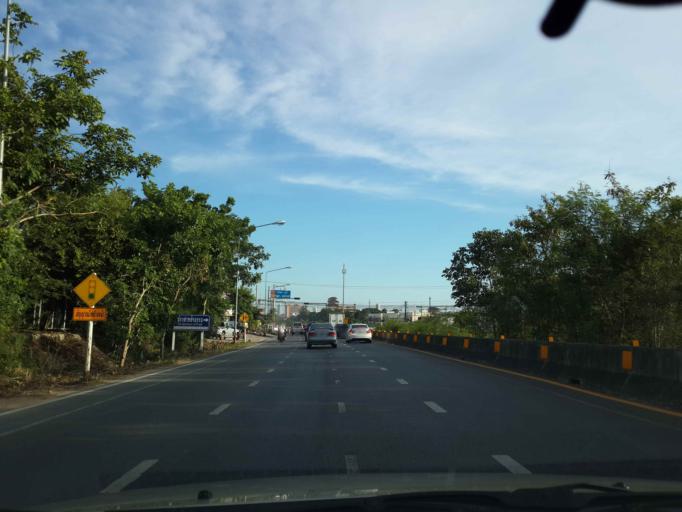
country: TH
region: Chon Buri
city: Phatthaya
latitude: 12.9267
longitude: 100.9035
